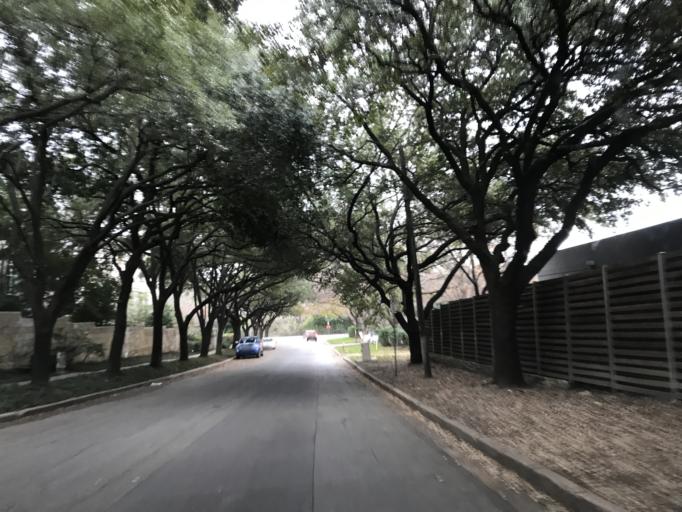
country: US
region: Texas
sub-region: Dallas County
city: Highland Park
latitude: 32.8162
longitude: -96.8003
